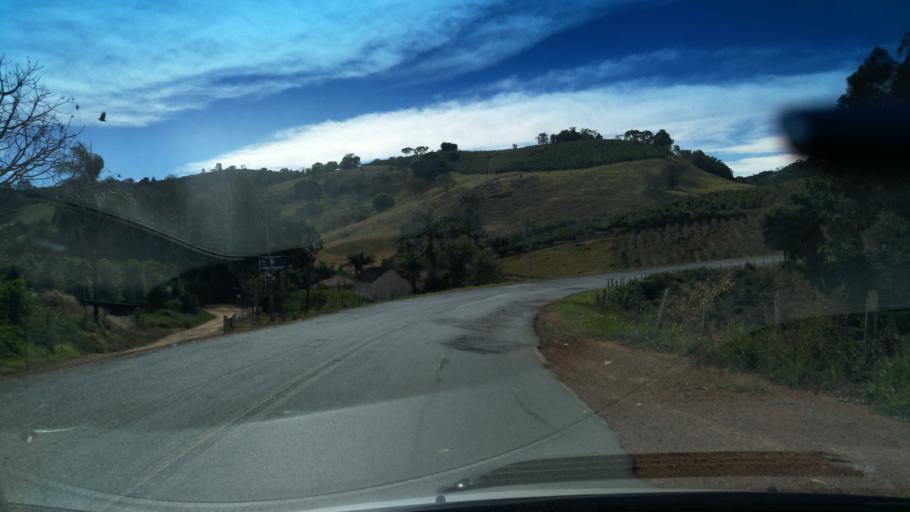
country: BR
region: Minas Gerais
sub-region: Andradas
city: Andradas
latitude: -22.0604
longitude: -46.3798
